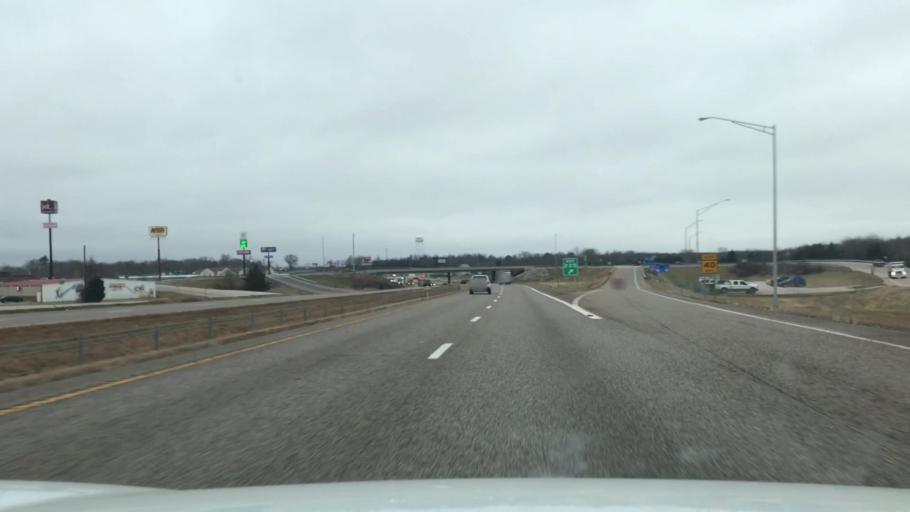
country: US
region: Missouri
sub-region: Franklin County
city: Sullivan
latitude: 38.2141
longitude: -91.1697
